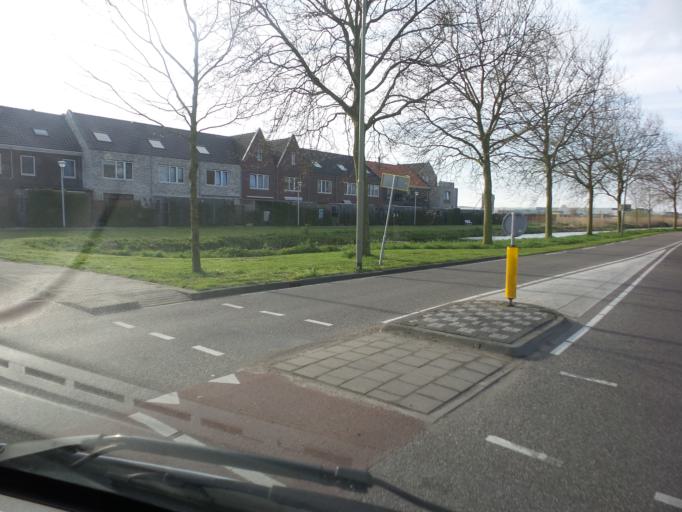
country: NL
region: South Holland
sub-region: Bodegraven-Reeuwijk
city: Bodegraven
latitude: 52.0761
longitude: 4.7601
